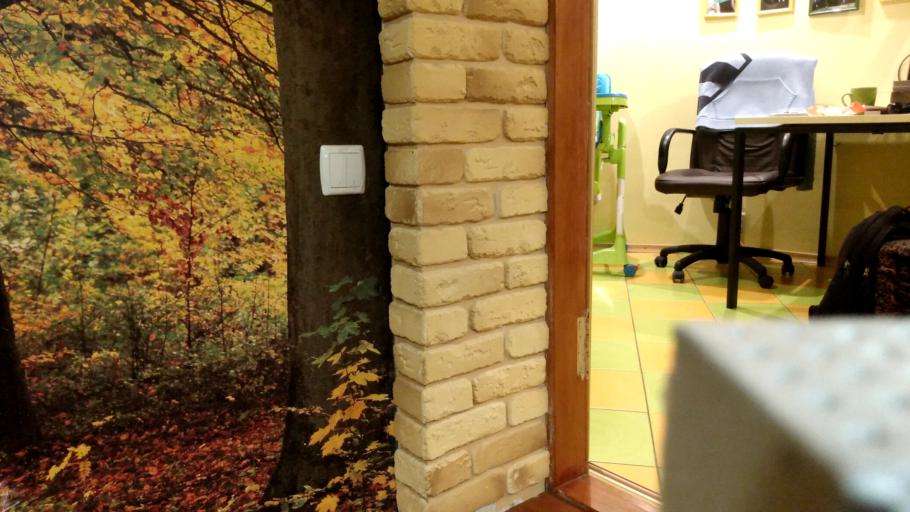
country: RU
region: Republic of Karelia
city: Pudozh
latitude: 61.7209
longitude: 37.7004
